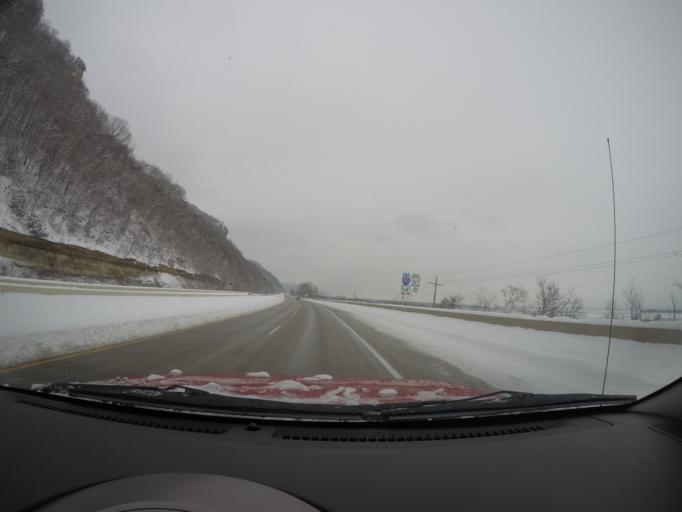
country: US
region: Minnesota
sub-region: Houston County
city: La Crescent
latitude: 43.8673
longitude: -91.3128
